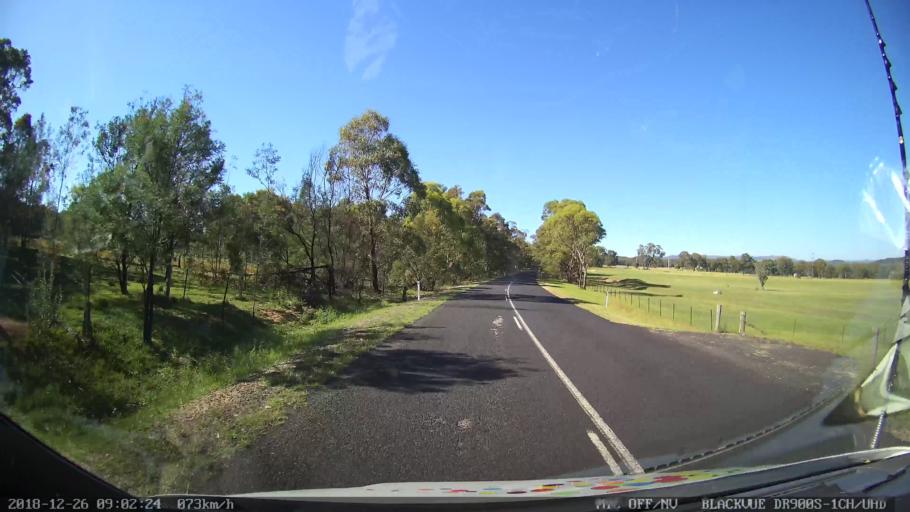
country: AU
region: New South Wales
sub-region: Mid-Western Regional
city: Kandos
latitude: -32.6524
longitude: 150.0192
